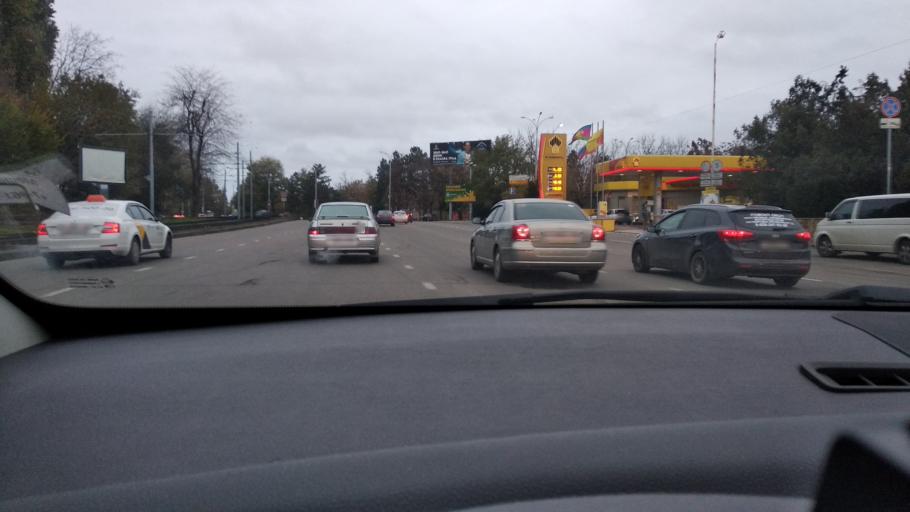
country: RU
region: Krasnodarskiy
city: Krasnodar
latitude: 45.0225
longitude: 38.9971
